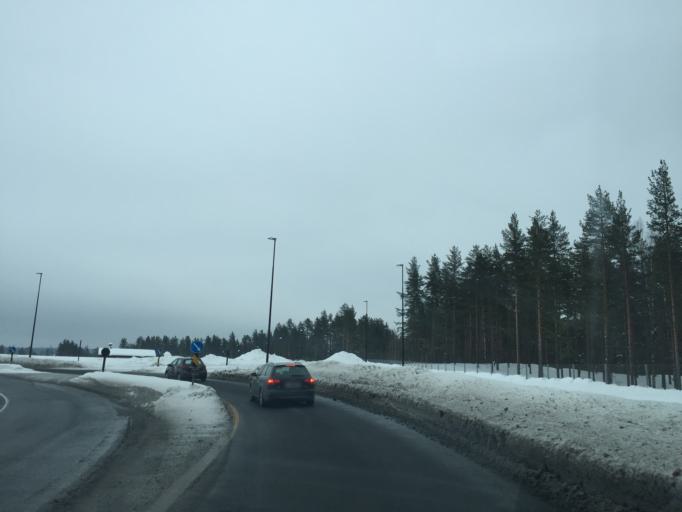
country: NO
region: Hedmark
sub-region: Elverum
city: Elverum
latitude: 60.8838
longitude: 11.5246
